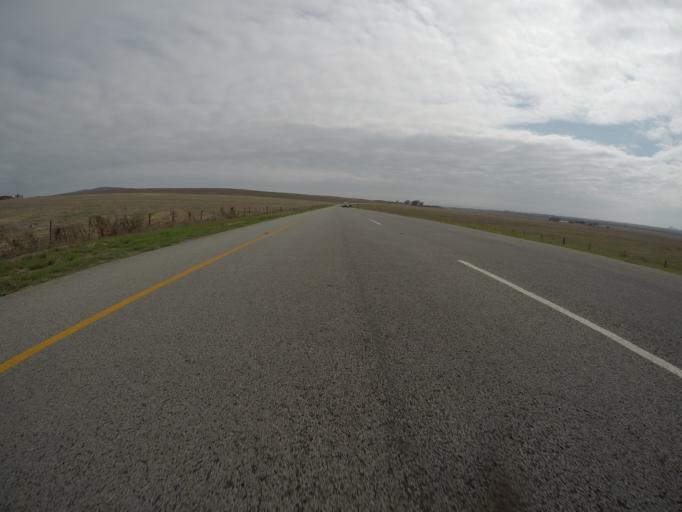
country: ZA
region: Western Cape
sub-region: City of Cape Town
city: Sunset Beach
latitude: -33.7261
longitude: 18.4866
